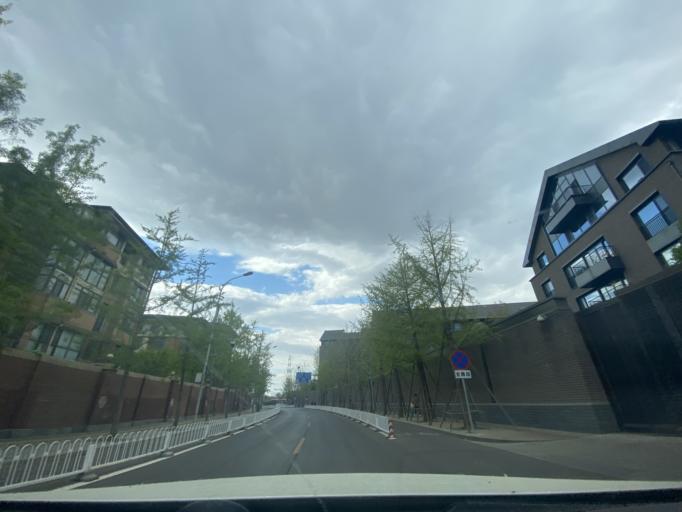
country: CN
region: Beijing
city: Haidian
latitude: 39.9713
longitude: 116.2861
